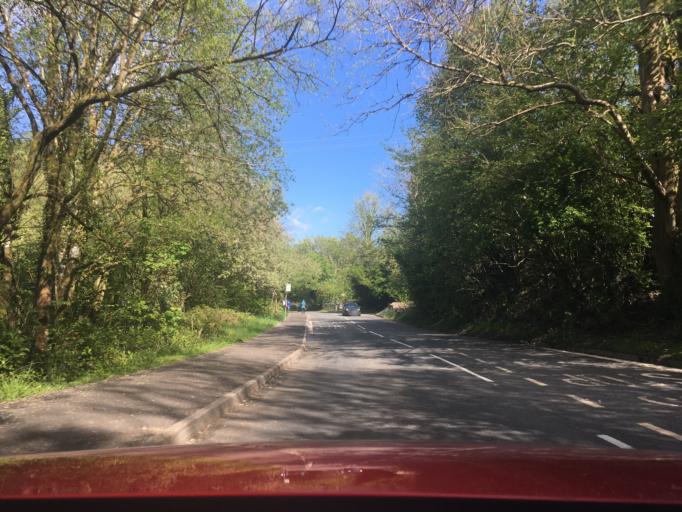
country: GB
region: Wales
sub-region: Caerphilly County Borough
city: Caerphilly
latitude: 51.5702
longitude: -3.1988
